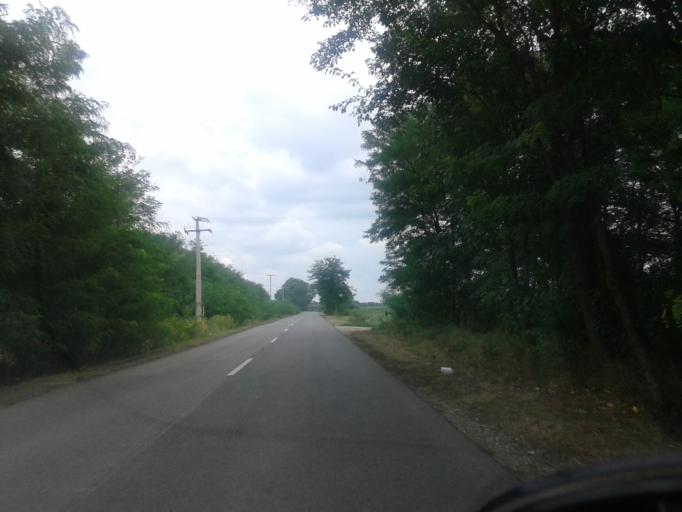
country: HU
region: Csongrad
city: Morahalom
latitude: 46.2052
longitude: 19.9158
